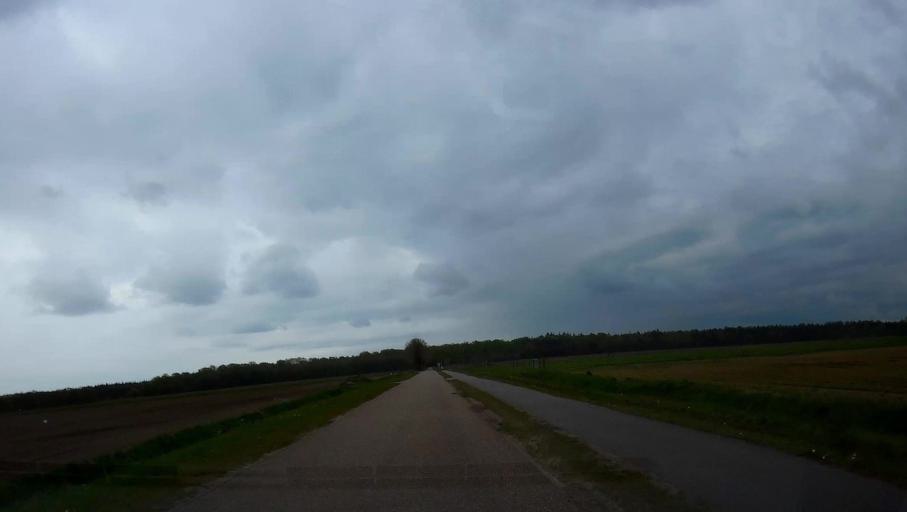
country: NL
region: Drenthe
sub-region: Gemeente Borger-Odoorn
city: Borger
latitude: 52.9721
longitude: 6.7713
